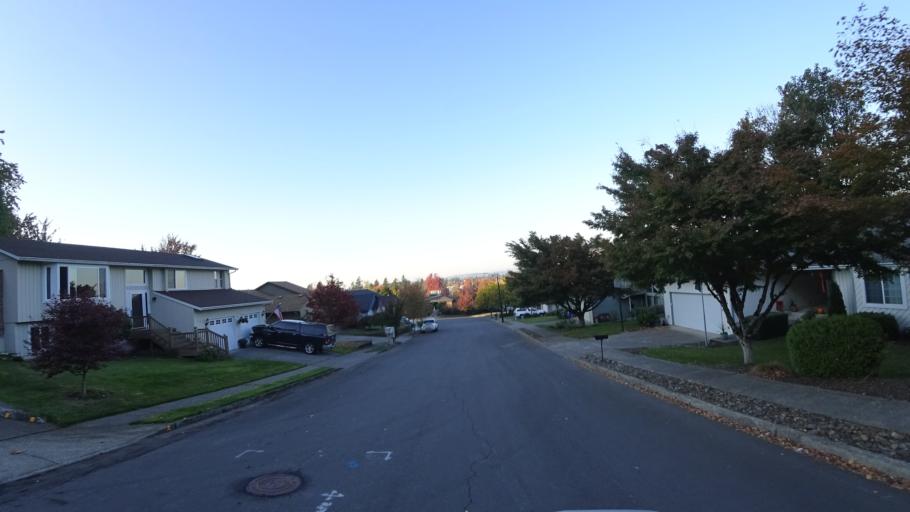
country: US
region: Oregon
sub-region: Multnomah County
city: Gresham
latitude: 45.4919
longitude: -122.4325
